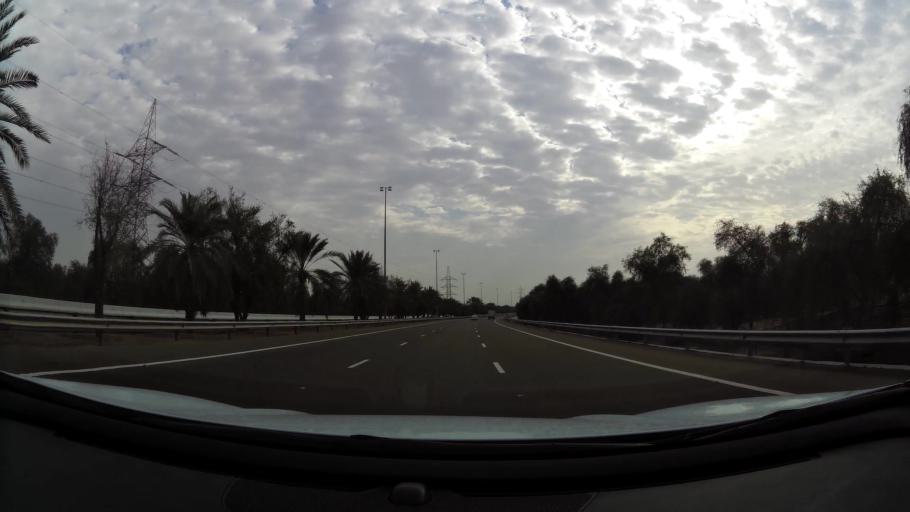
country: AE
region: Abu Dhabi
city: Al Ain
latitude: 24.1718
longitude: 55.2310
